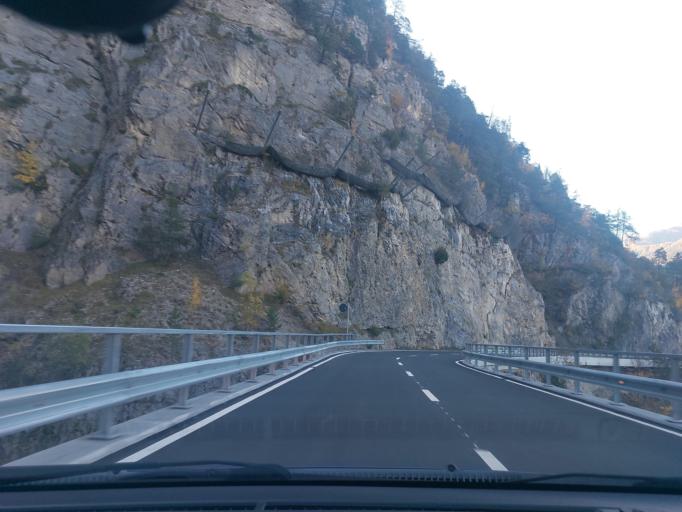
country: CH
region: Valais
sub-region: Sierre District
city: Chippis
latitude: 46.2564
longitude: 7.5755
